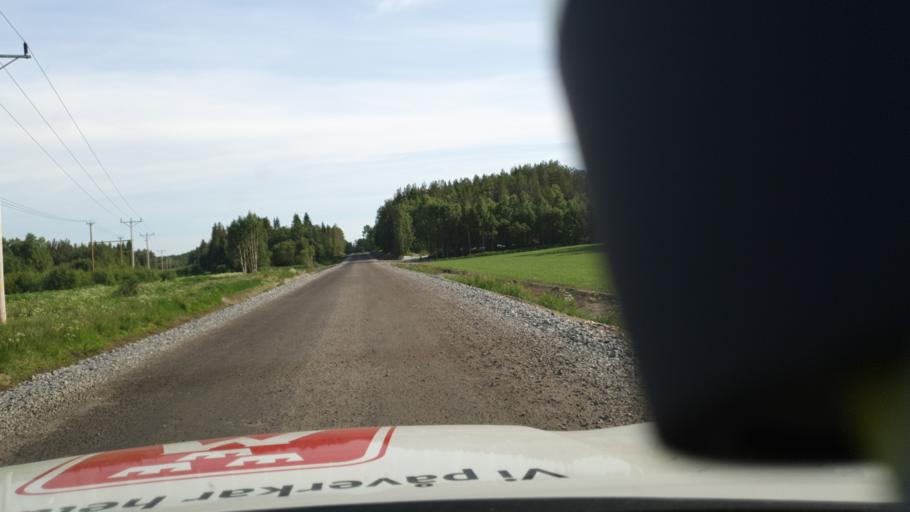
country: SE
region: Vaesterbotten
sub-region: Robertsfors Kommun
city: Robertsfors
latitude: 64.2936
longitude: 21.0325
